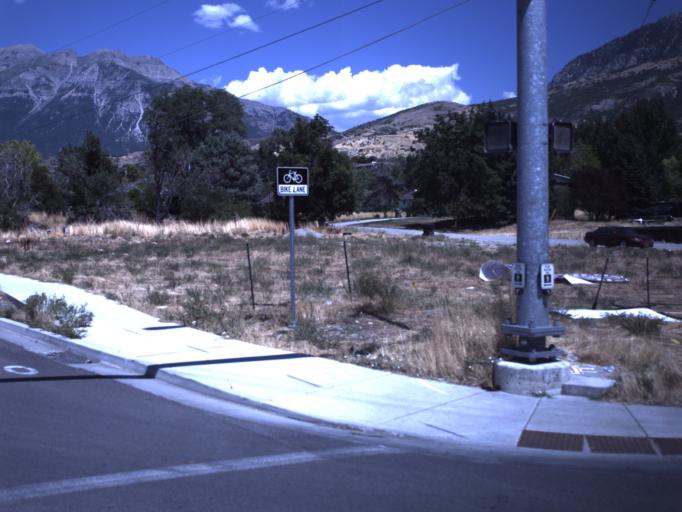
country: US
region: Utah
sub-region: Utah County
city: Orem
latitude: 40.2829
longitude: -111.6584
